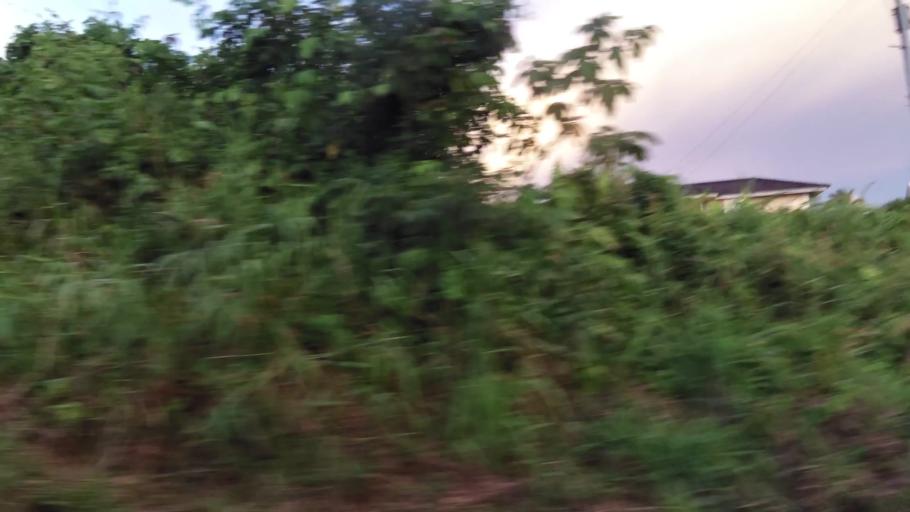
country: BN
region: Brunei and Muara
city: Bandar Seri Begawan
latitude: 5.0003
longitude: 114.9984
